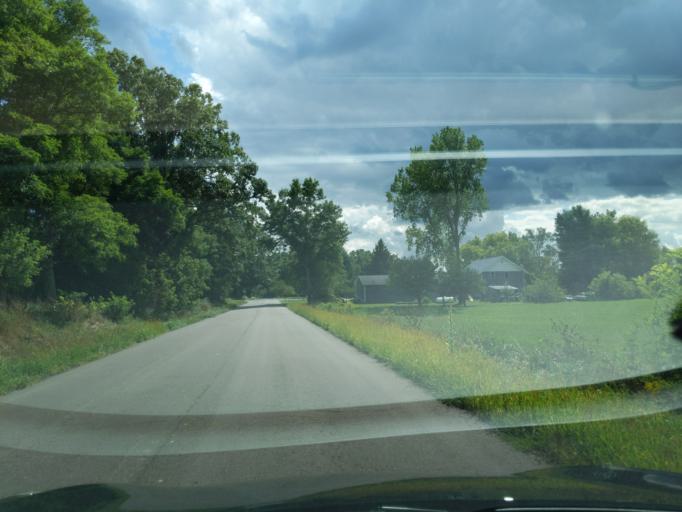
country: US
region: Michigan
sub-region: Eaton County
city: Eaton Rapids
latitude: 42.4669
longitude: -84.5805
